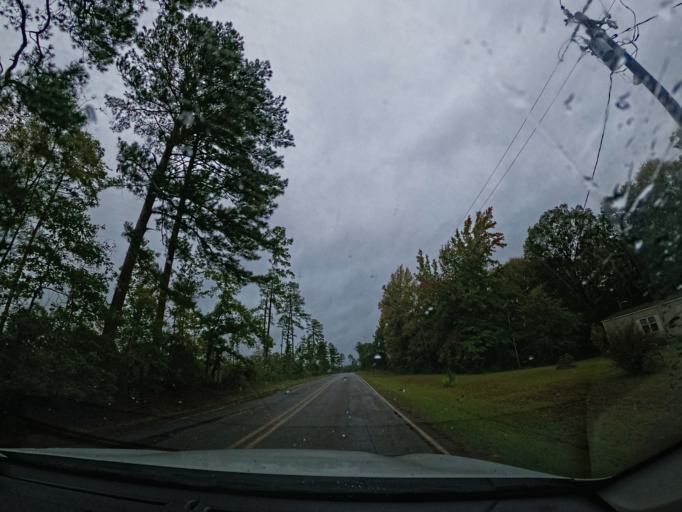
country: US
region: Louisiana
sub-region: Webster Parish
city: Minden
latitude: 32.6857
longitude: -93.2474
